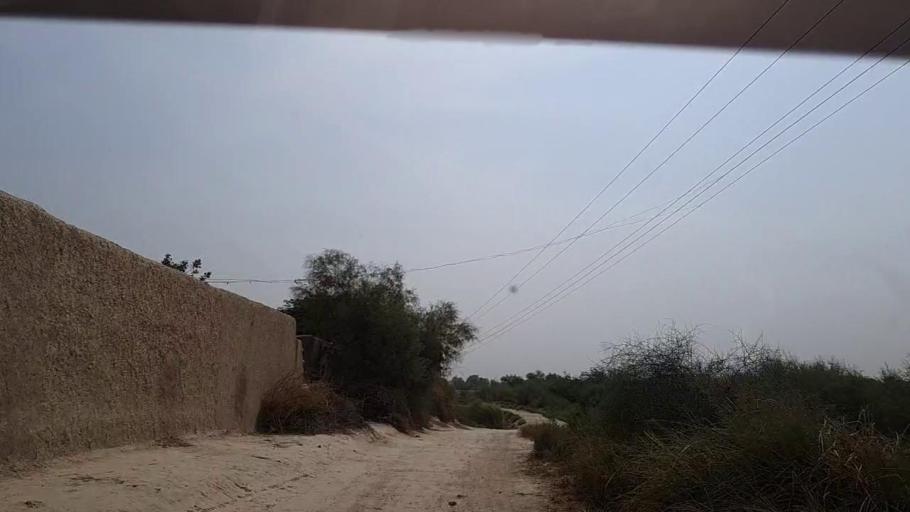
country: PK
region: Sindh
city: Khairpur Nathan Shah
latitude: 27.0268
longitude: 67.6745
